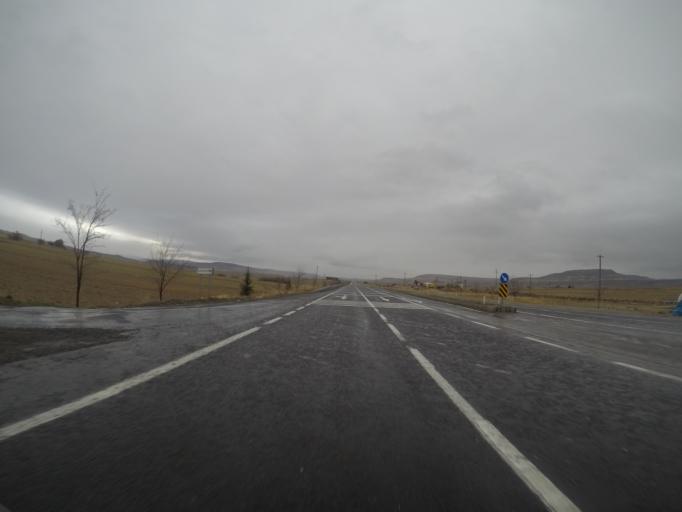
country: TR
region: Nevsehir
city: Urgub
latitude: 38.7175
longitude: 34.9396
